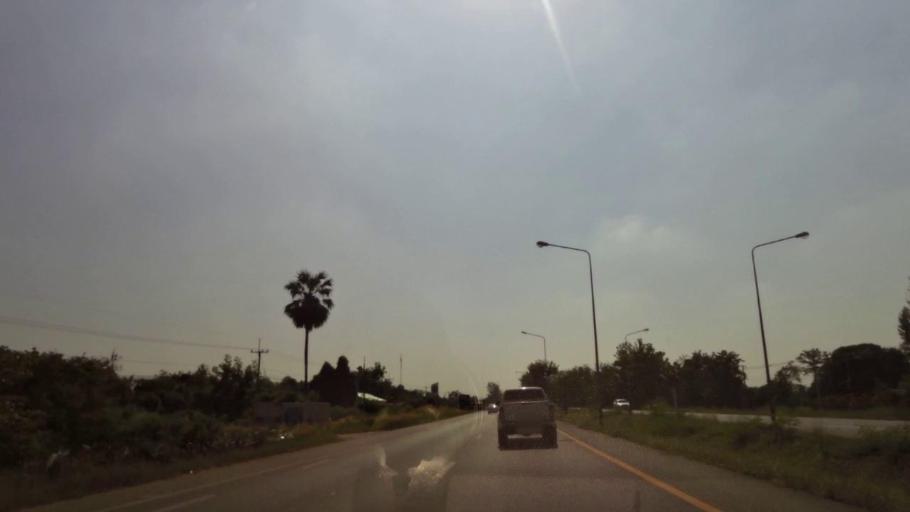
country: TH
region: Phichit
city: Wachira Barami
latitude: 16.4247
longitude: 100.1444
